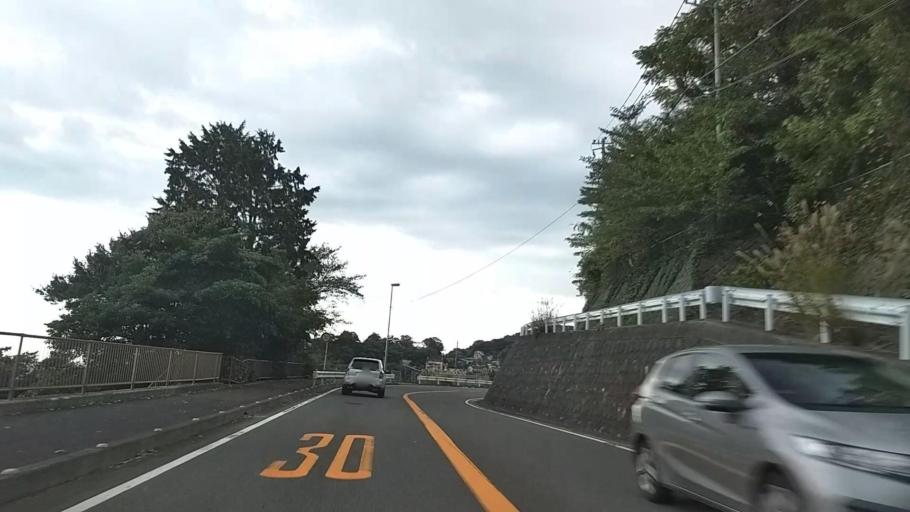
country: JP
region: Kanagawa
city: Odawara
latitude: 35.1945
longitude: 139.1340
